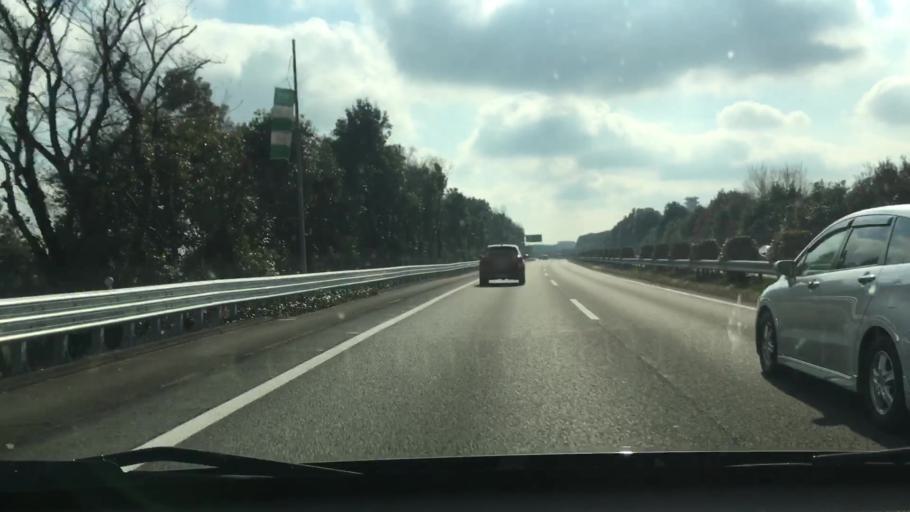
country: JP
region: Kumamoto
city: Ozu
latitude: 32.8032
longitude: 130.7926
